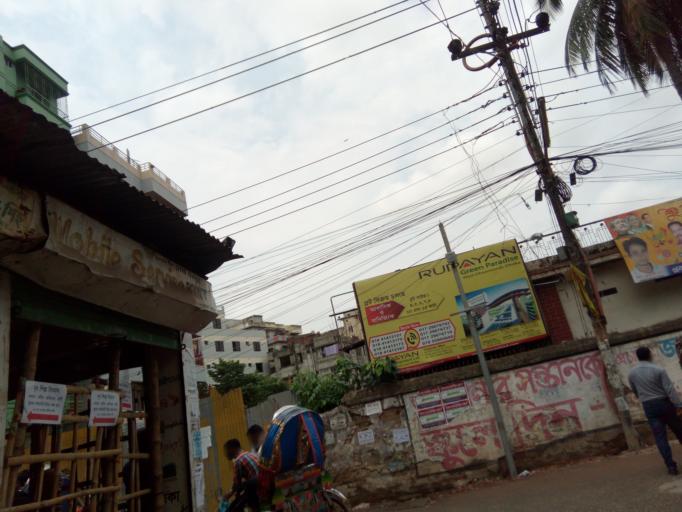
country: BD
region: Dhaka
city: Azimpur
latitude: 23.7469
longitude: 90.3647
